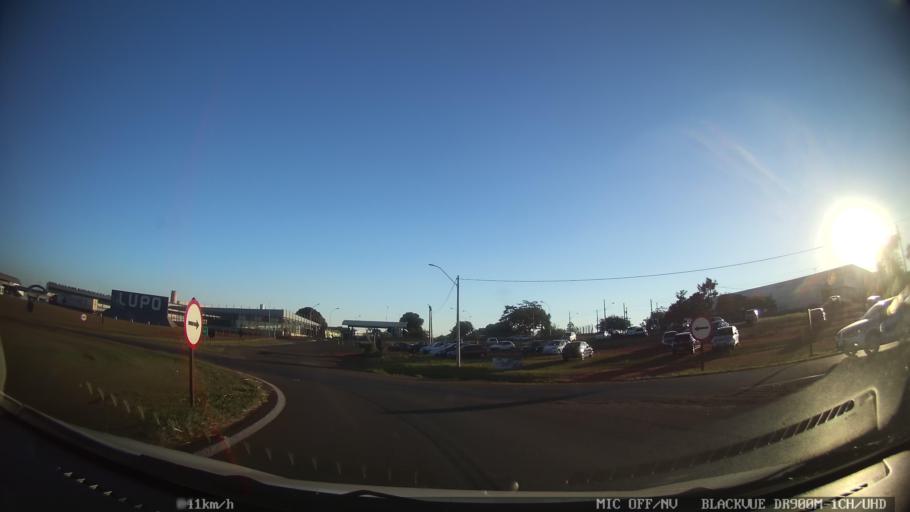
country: BR
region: Sao Paulo
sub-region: Araraquara
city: Araraquara
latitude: -21.7880
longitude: -48.2205
